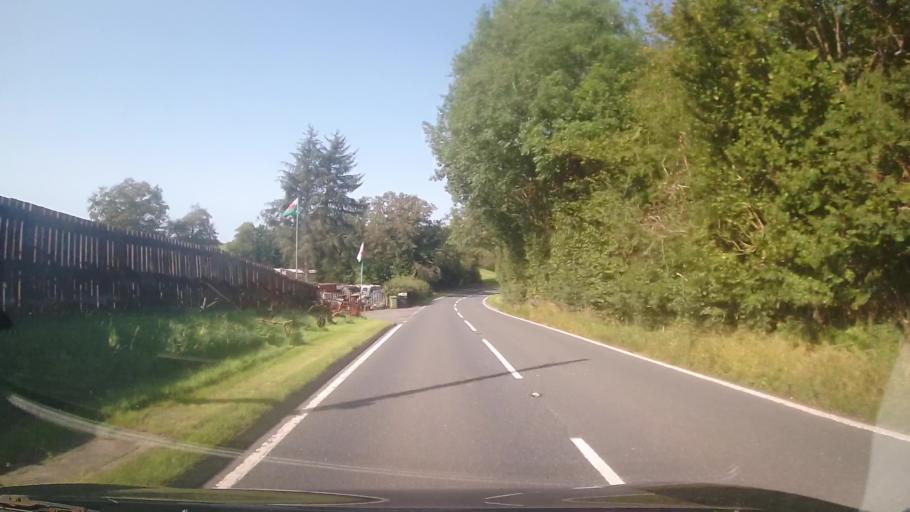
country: GB
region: Wales
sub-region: Sir Powys
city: Builth Wells
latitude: 52.1402
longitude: -3.5683
